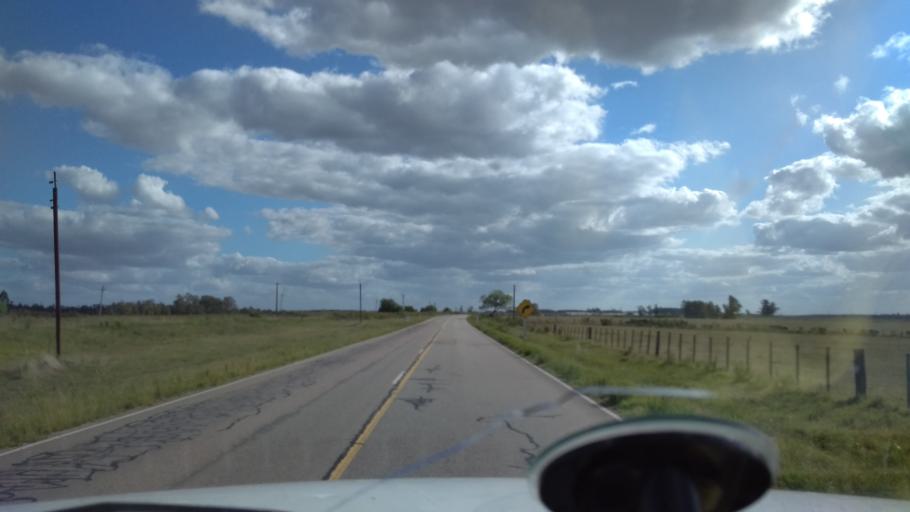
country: UY
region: Florida
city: Casupa
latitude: -34.1506
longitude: -55.6835
